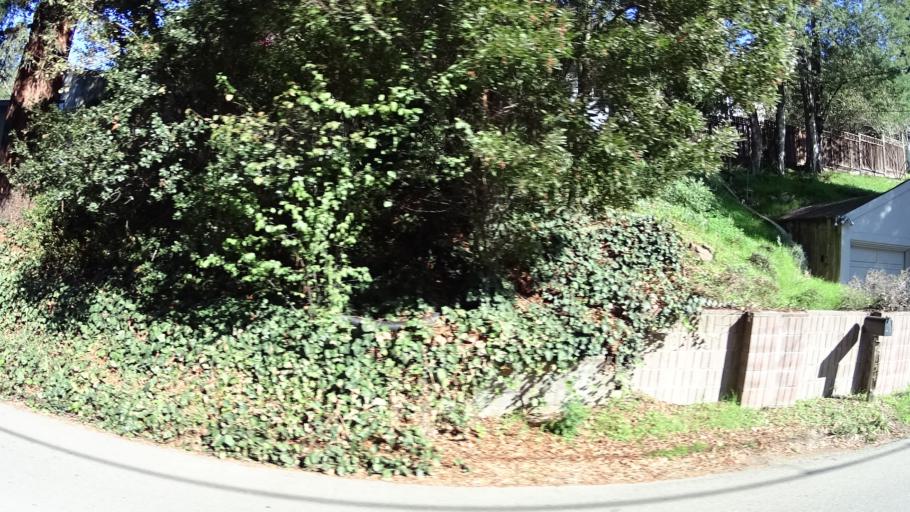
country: US
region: California
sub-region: Alameda County
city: Piedmont
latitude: 37.8381
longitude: -122.2199
